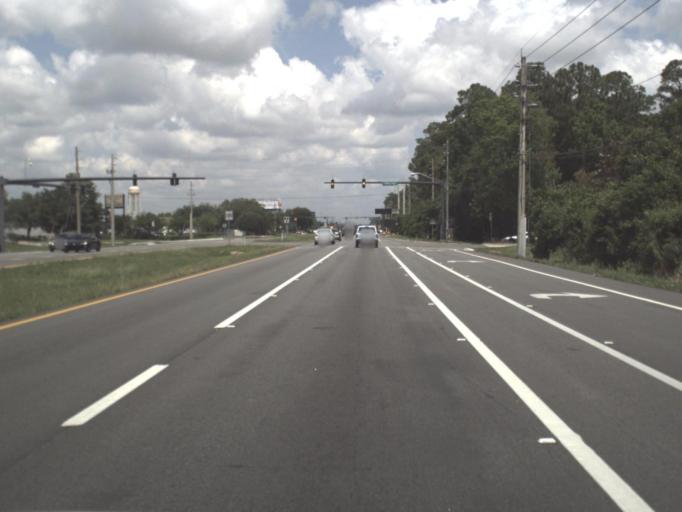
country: US
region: Florida
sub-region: Saint Johns County
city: Fruit Cove
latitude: 30.2132
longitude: -81.5814
